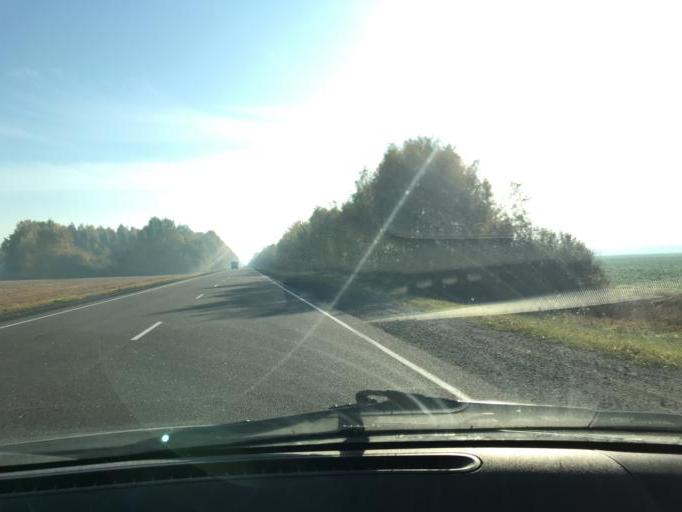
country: BY
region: Brest
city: Horad Luninyets
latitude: 52.3037
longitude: 26.7058
